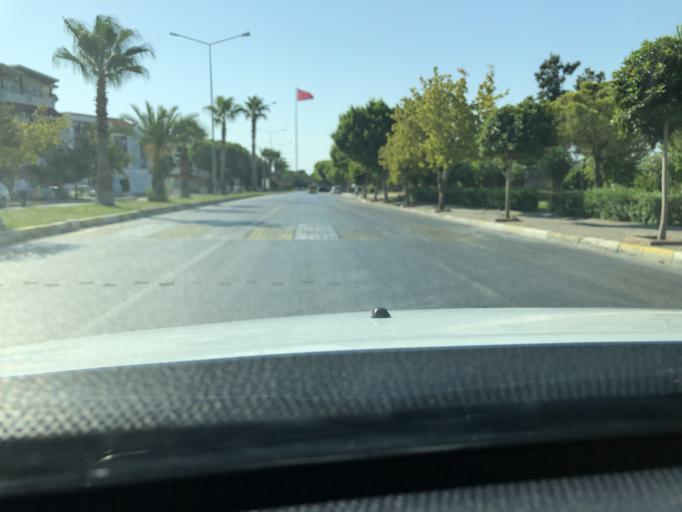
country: TR
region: Antalya
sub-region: Manavgat
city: Side
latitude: 36.7791
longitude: 31.3951
